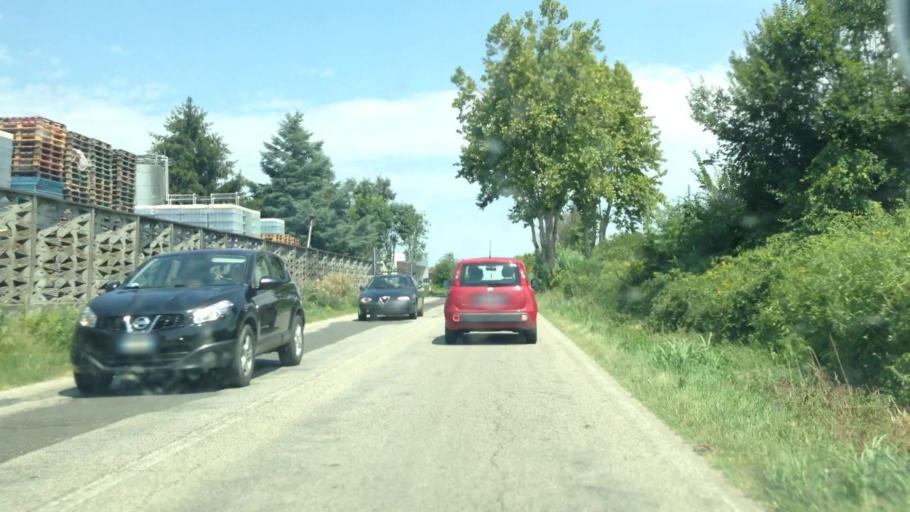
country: IT
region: Piedmont
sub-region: Provincia di Asti
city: Portacomaro
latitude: 44.9388
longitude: 8.2247
